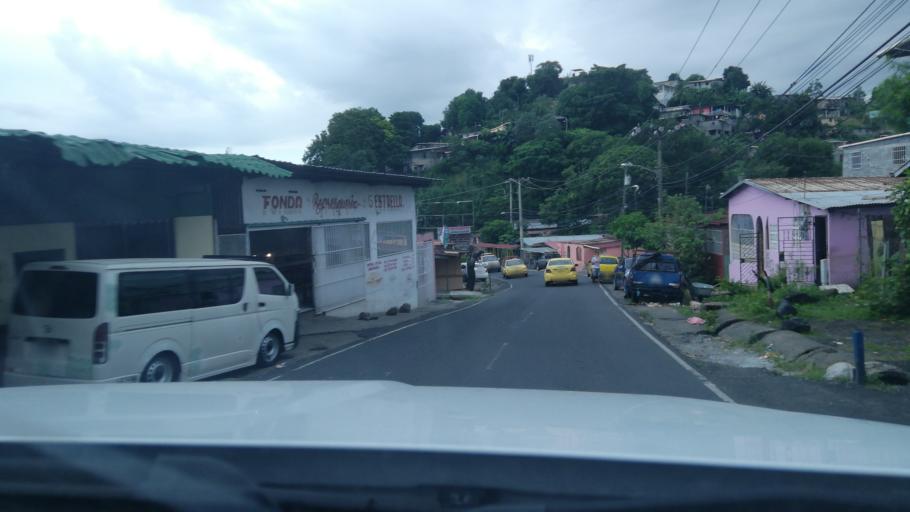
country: PA
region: Panama
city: San Miguelito
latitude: 9.0474
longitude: -79.4929
